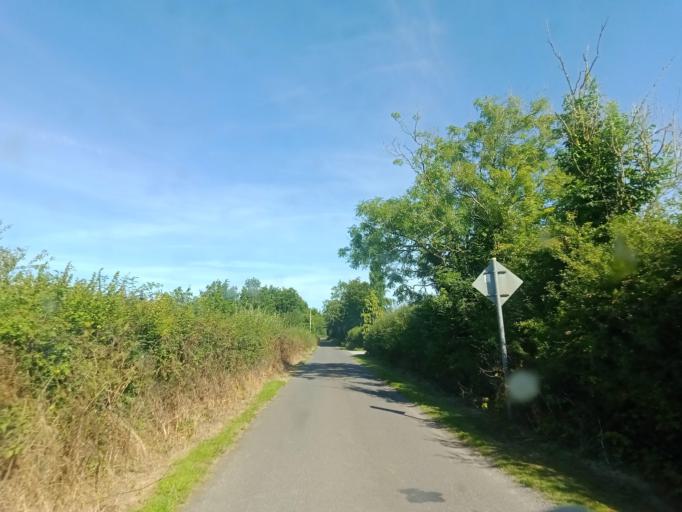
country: IE
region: Leinster
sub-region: Kilkenny
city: Ballyragget
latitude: 52.7847
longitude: -7.4198
